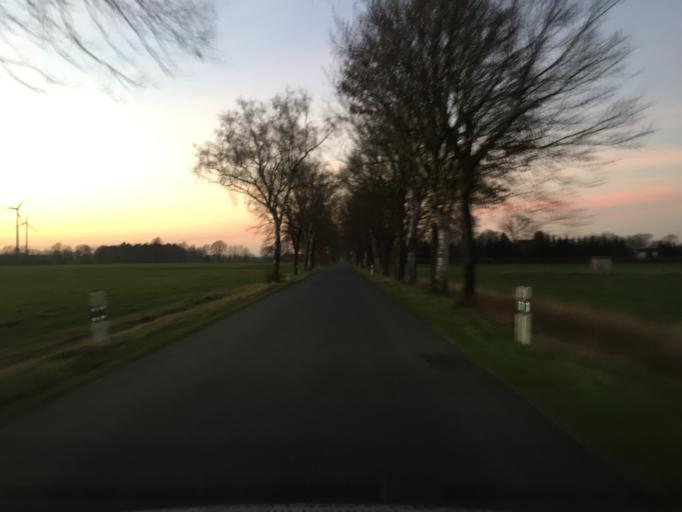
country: DE
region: Lower Saxony
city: Barenburg
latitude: 52.6405
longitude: 8.8363
